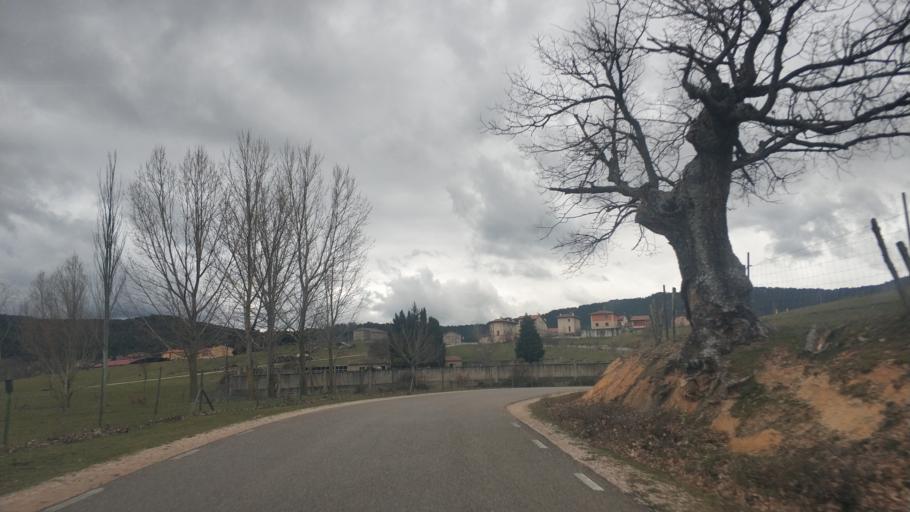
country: ES
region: Castille and Leon
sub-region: Provincia de Burgos
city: Canicosa de la Sierra
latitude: 41.9411
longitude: -3.0368
